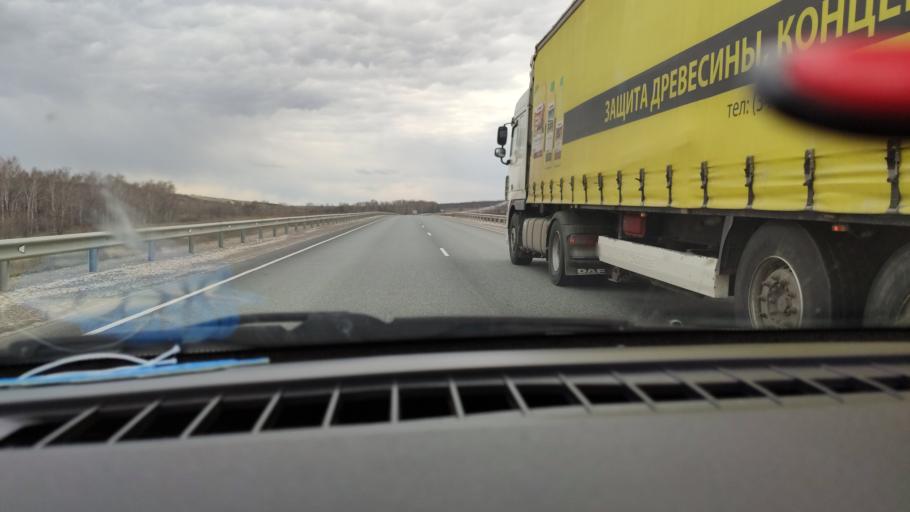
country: RU
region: Saratov
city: Yelshanka
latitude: 51.8569
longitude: 46.4955
